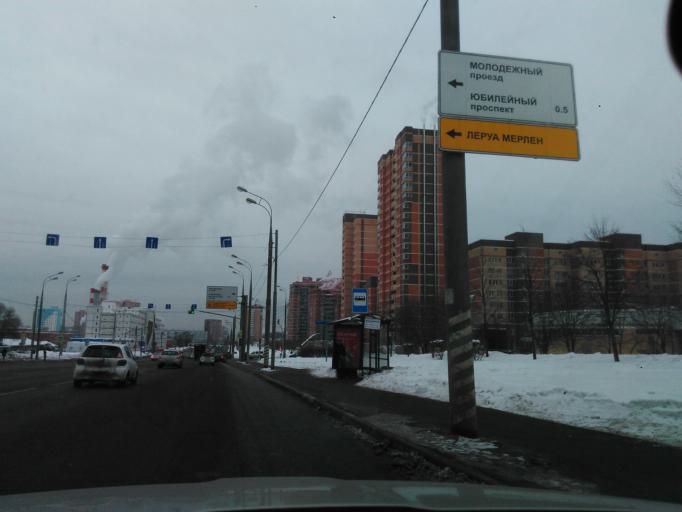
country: RU
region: Moscow
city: Khimki
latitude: 55.8994
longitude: 37.3987
